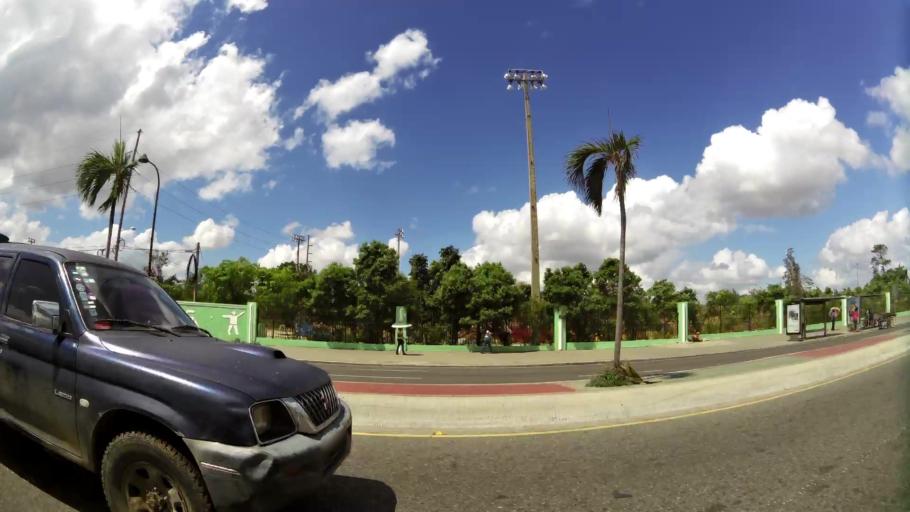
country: DO
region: Nacional
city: San Carlos
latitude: 18.4805
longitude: -69.9141
